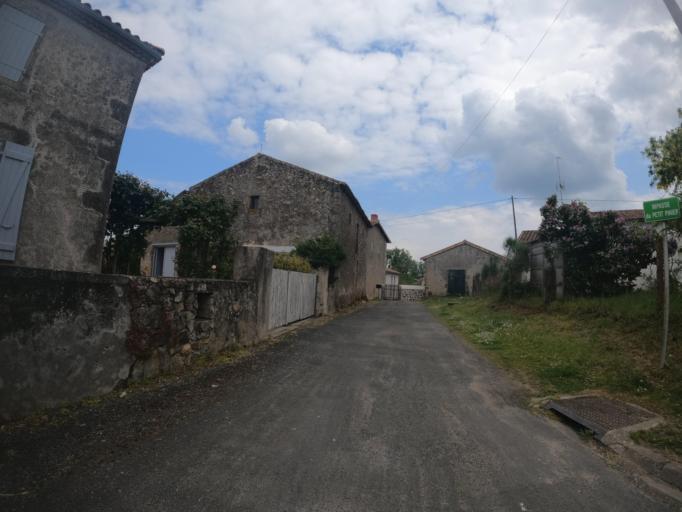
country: FR
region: Poitou-Charentes
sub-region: Departement des Deux-Sevres
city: Saint-Varent
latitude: 46.8676
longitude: -0.3004
